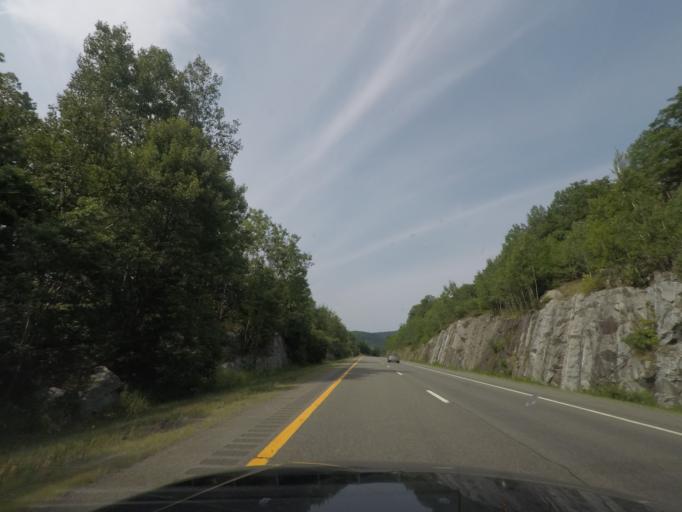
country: US
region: New York
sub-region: Essex County
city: Keeseville
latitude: 44.3636
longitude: -73.5297
